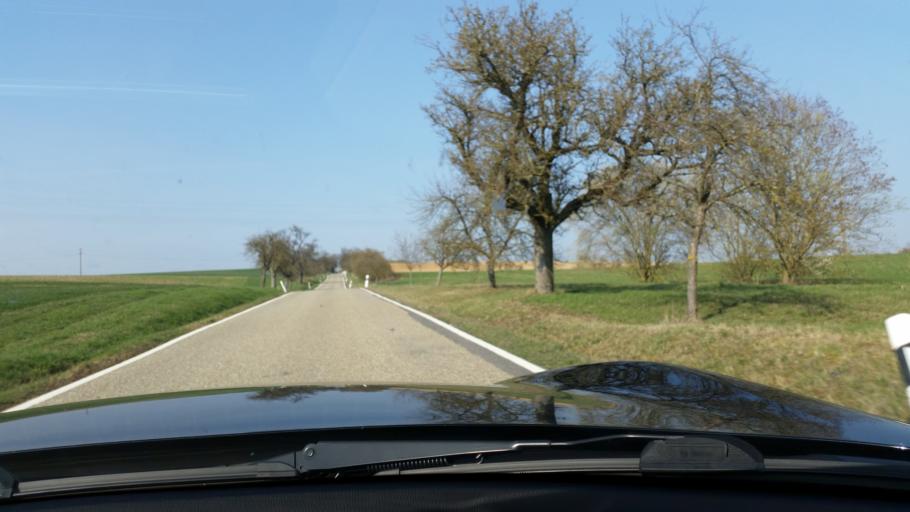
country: DE
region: Baden-Wuerttemberg
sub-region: Regierungsbezirk Stuttgart
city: Mockmuhl
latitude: 49.3308
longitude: 9.3659
